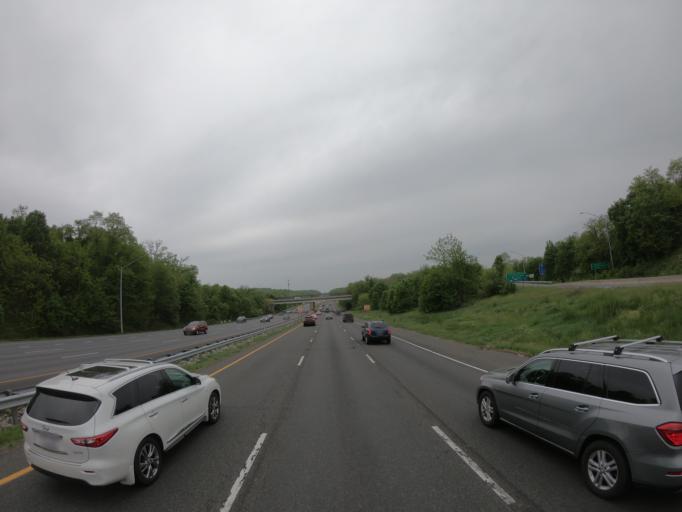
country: US
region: Maryland
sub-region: Anne Arundel County
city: Arnold
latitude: 39.0224
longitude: -76.4741
